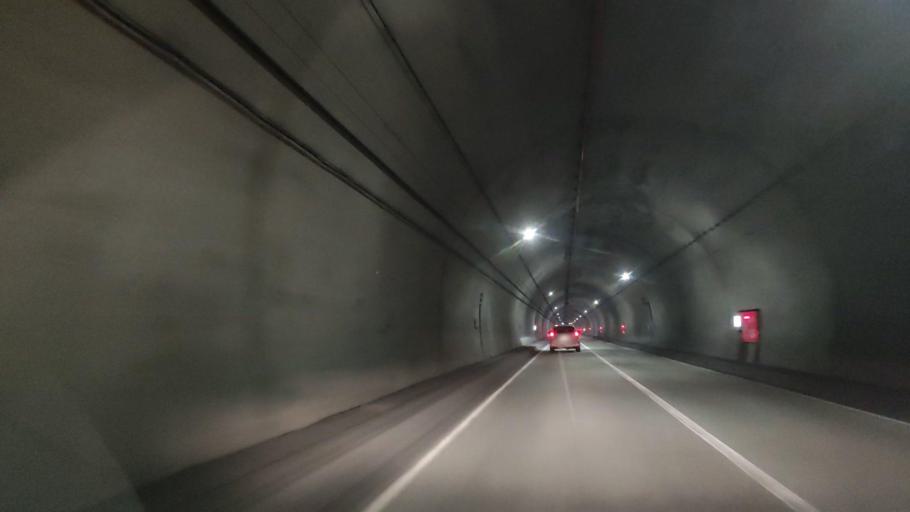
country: JP
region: Hokkaido
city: Rumoi
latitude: 43.7154
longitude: 141.3299
